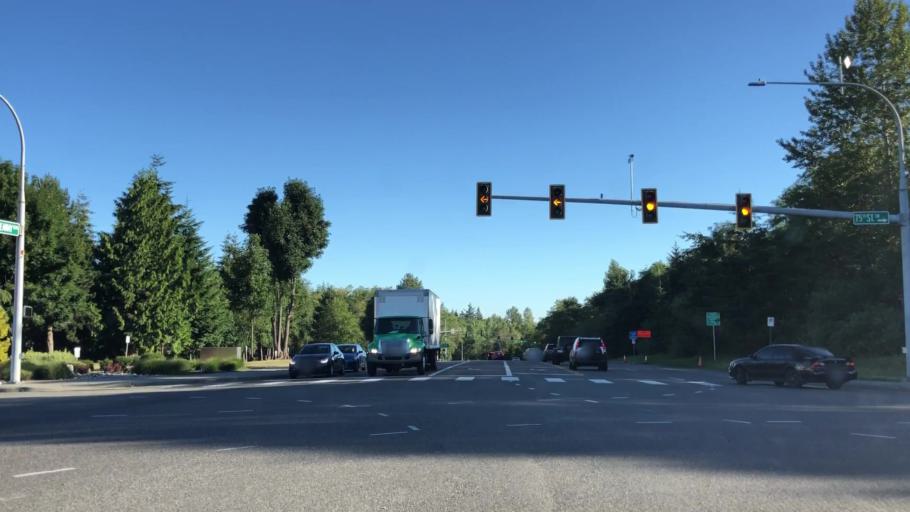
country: US
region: Washington
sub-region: Snohomish County
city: Mukilteo
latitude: 47.9309
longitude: -122.2608
